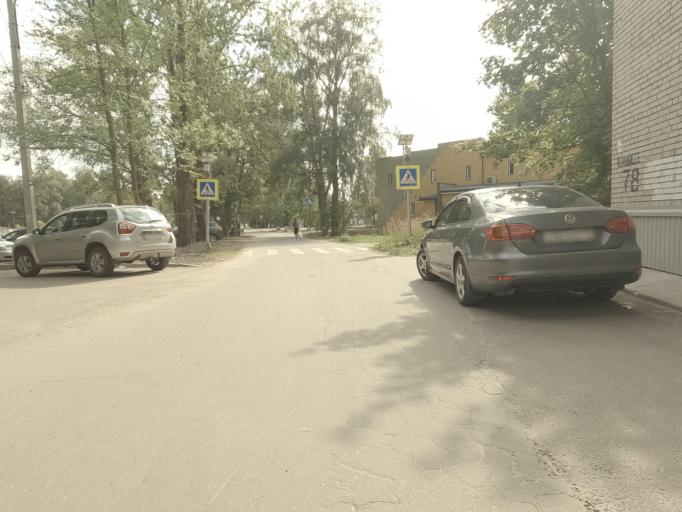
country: RU
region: Leningrad
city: Kamennogorsk
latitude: 60.9541
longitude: 29.1312
